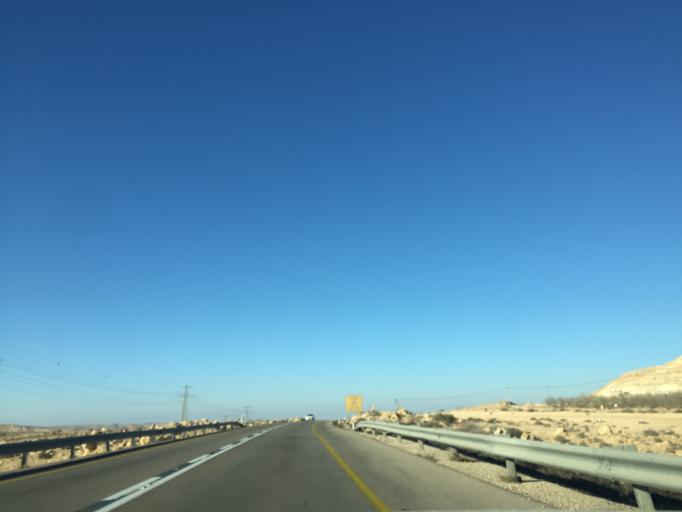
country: IL
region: Southern District
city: Midreshet Ben-Gurion
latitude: 30.7861
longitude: 34.7682
